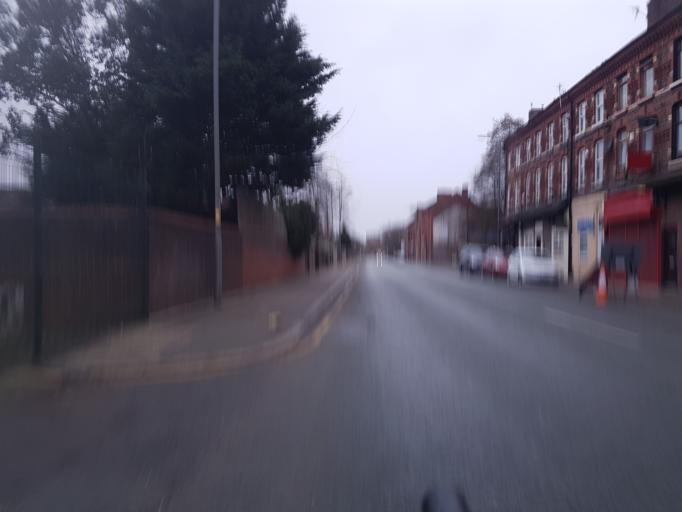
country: GB
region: England
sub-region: Liverpool
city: Liverpool
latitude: 53.4355
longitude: -2.9755
